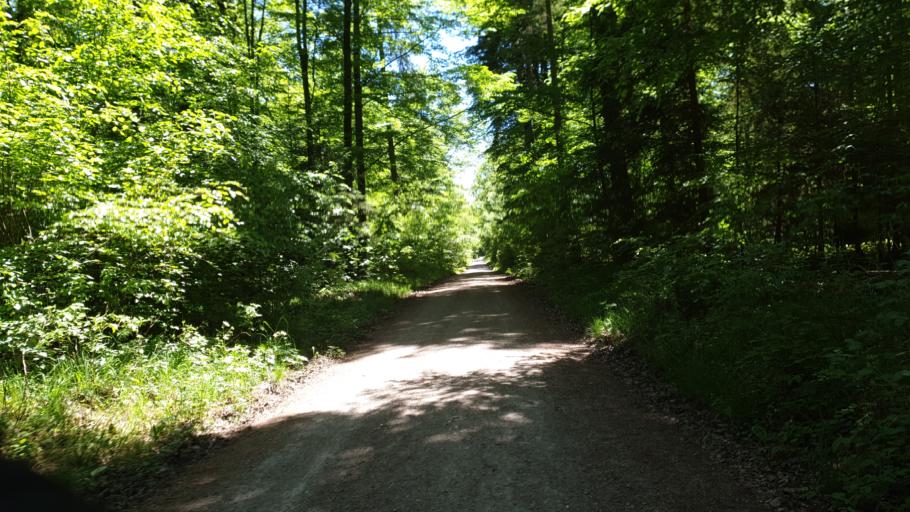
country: DE
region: Bavaria
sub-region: Upper Bavaria
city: Seeshaupt
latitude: 47.7955
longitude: 11.2854
